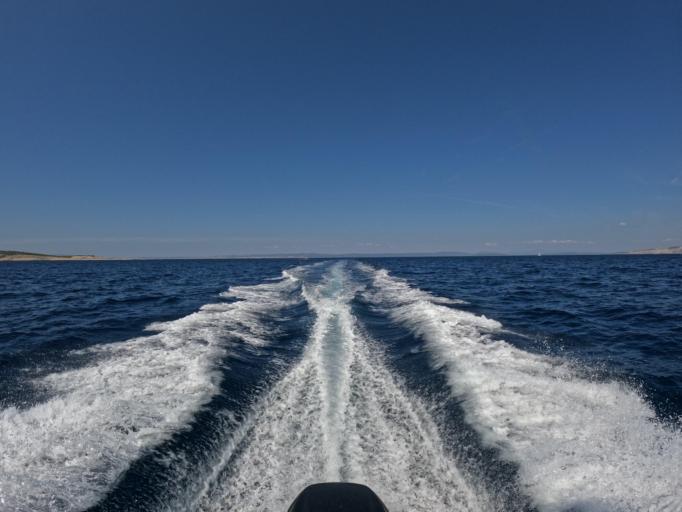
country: HR
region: Primorsko-Goranska
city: Lopar
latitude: 44.8544
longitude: 14.7082
